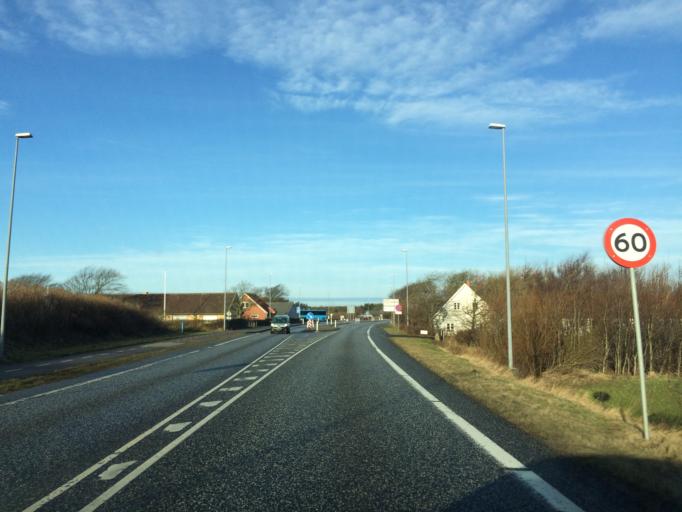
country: DK
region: Central Jutland
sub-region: Struer Kommune
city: Struer
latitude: 56.5381
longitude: 8.5614
